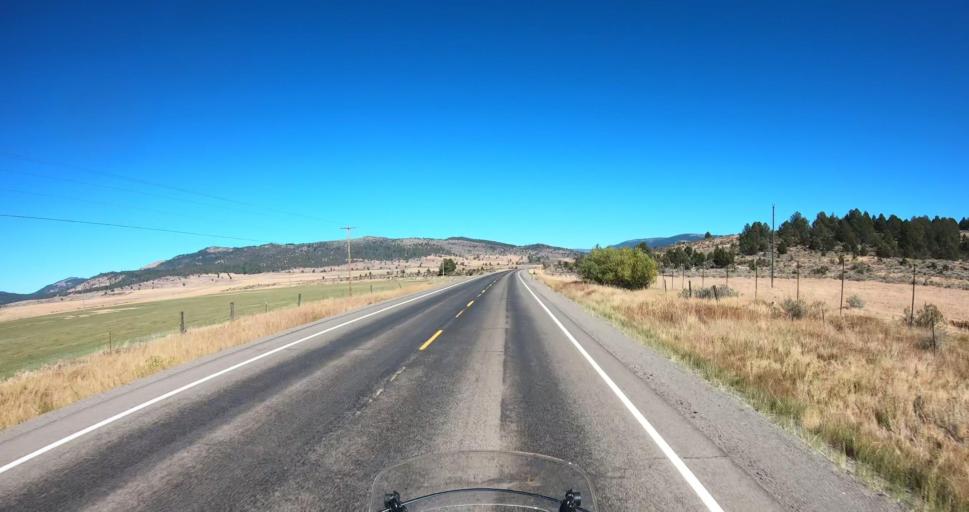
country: US
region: Oregon
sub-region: Lake County
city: Lakeview
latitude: 42.3129
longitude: -120.3389
